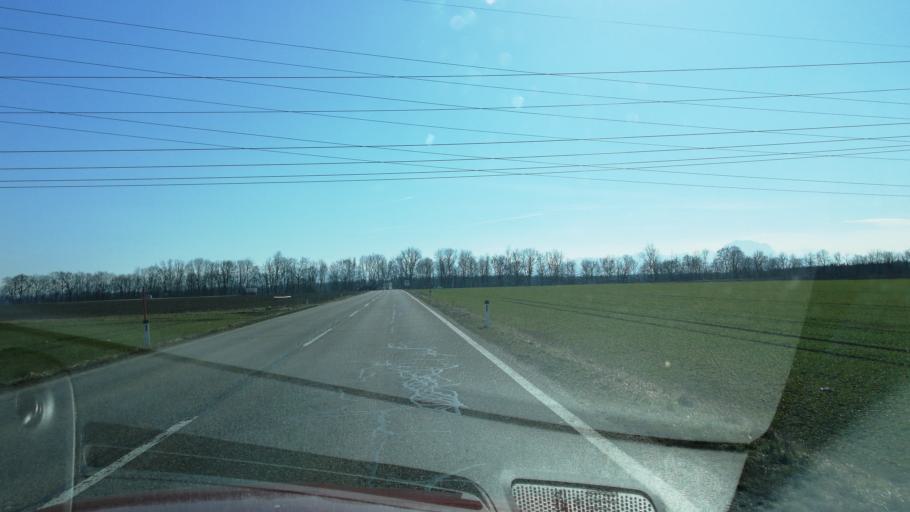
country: AT
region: Upper Austria
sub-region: Wels-Land
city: Neukirchen bei Lambach
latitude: 48.0911
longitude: 13.8397
